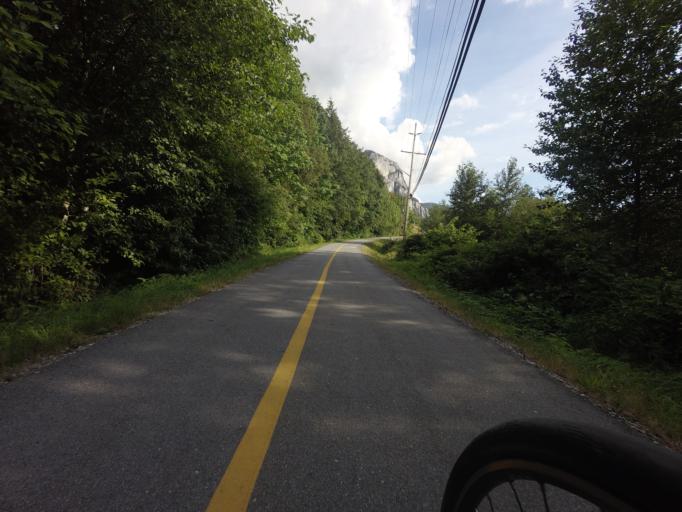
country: CA
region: British Columbia
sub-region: Greater Vancouver Regional District
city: Lions Bay
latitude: 49.6980
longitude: -123.1431
